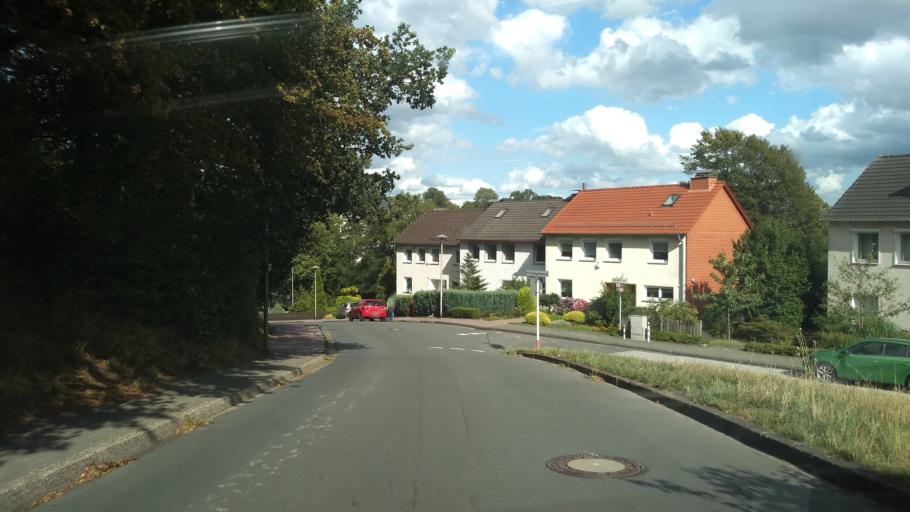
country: DE
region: North Rhine-Westphalia
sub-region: Regierungsbezirk Arnsberg
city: Luedenscheid
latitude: 51.2249
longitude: 7.5999
